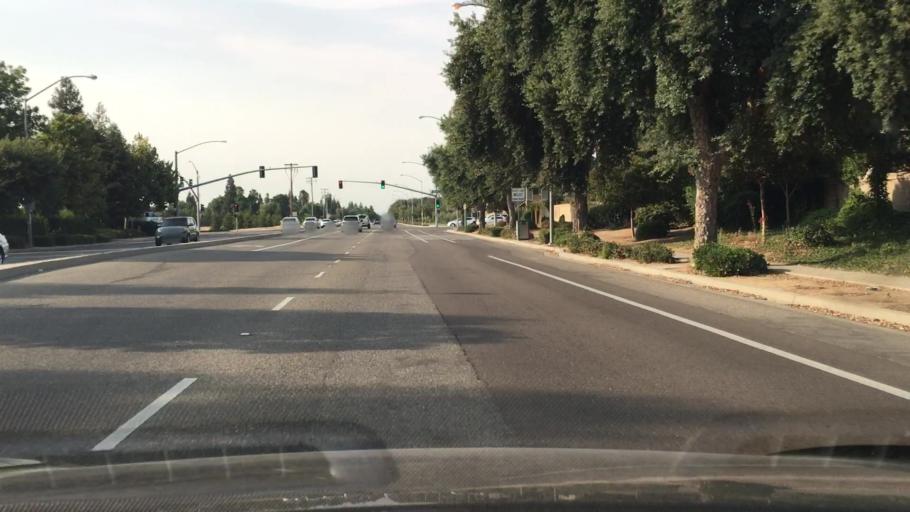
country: US
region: California
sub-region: Fresno County
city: Clovis
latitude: 36.8511
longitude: -119.7387
